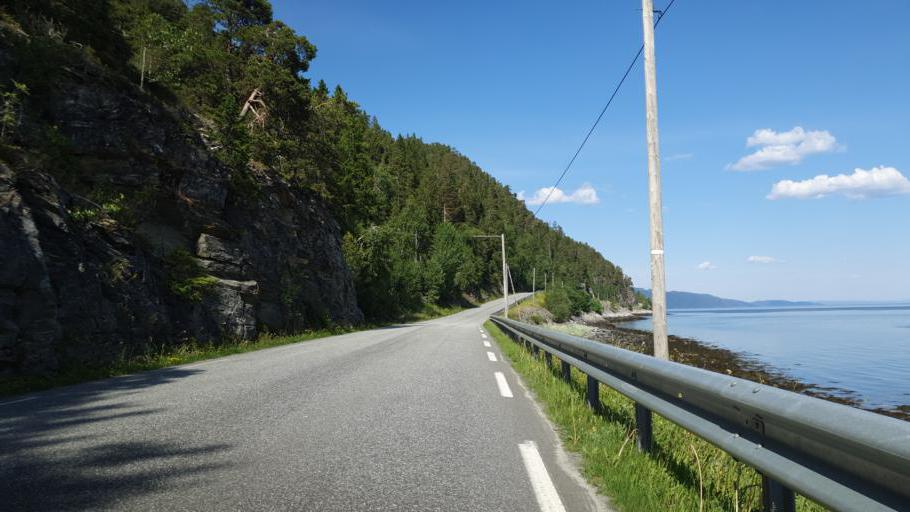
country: NO
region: Nord-Trondelag
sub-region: Leksvik
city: Leksvik
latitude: 63.6417
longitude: 10.5909
